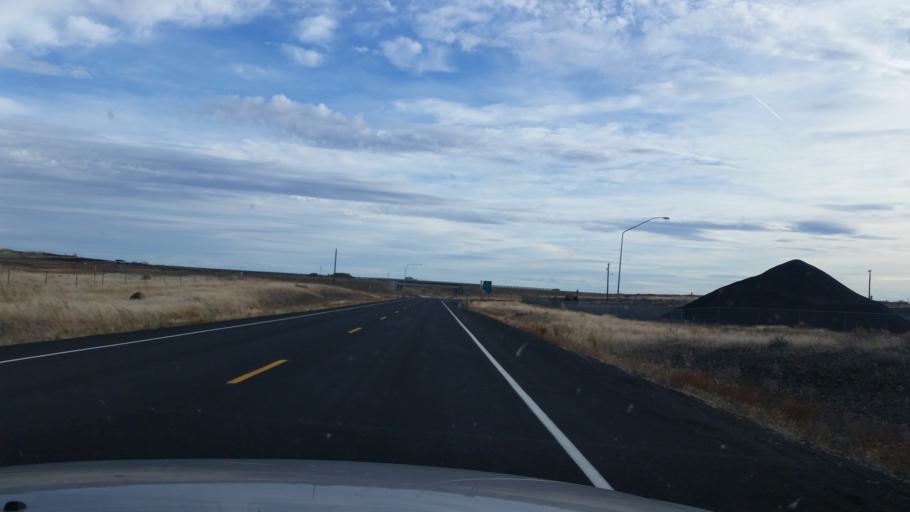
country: US
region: Washington
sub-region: Lincoln County
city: Davenport
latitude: 47.3117
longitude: -117.9732
